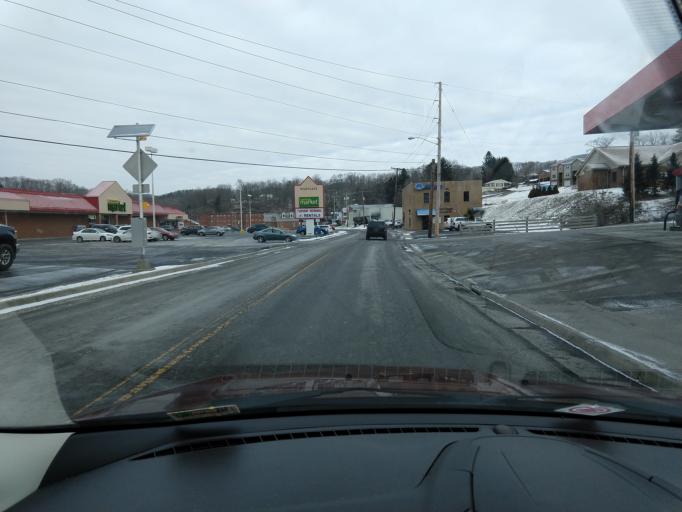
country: US
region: West Virginia
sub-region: Mercer County
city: Bluefield
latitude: 37.2434
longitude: -81.2391
